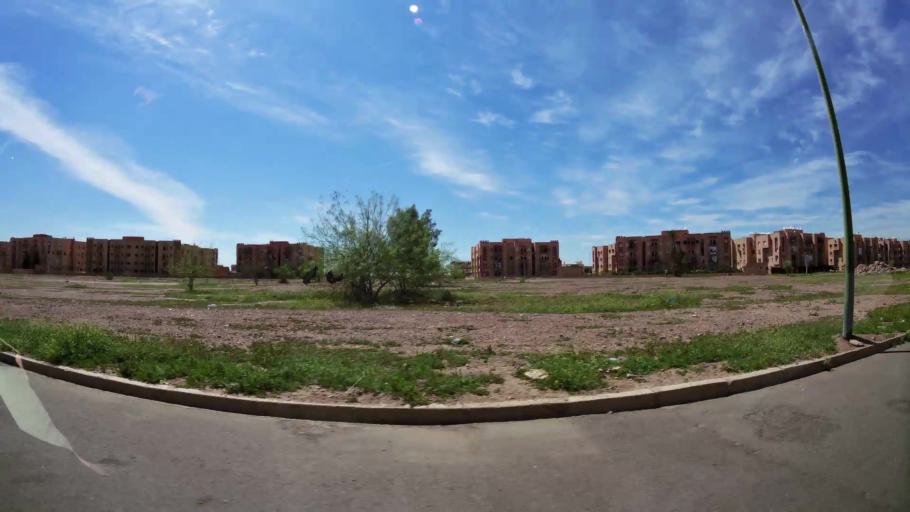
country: MA
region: Marrakech-Tensift-Al Haouz
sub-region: Marrakech
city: Marrakesh
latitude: 31.6441
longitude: -8.0789
